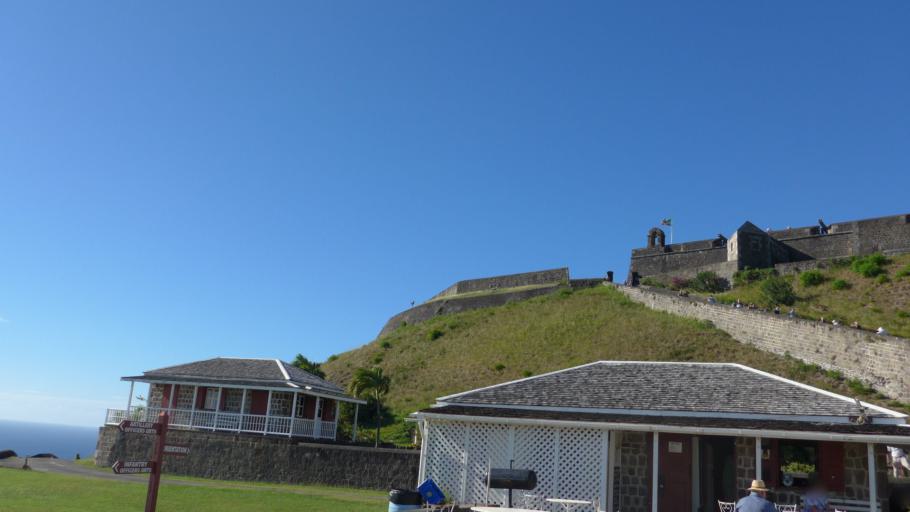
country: KN
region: Saint Anne Sandy Point
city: Sandy Point Town
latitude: 17.3469
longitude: -62.8358
